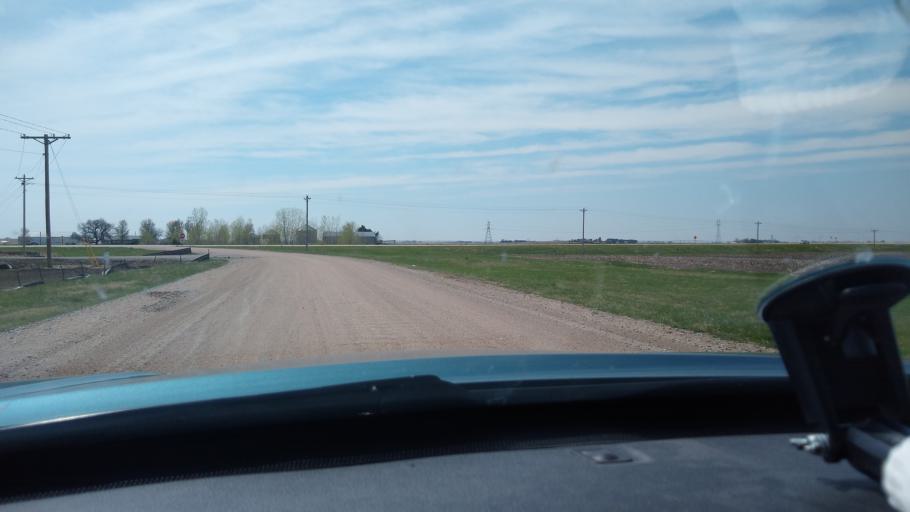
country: US
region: Nebraska
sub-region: Fillmore County
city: Geneva
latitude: 40.4155
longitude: -97.5923
